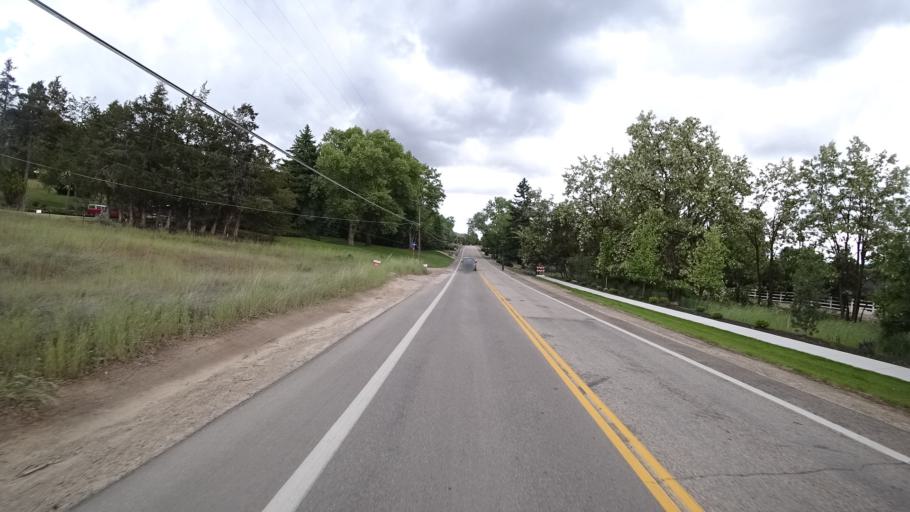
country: US
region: Idaho
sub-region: Ada County
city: Garden City
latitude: 43.6761
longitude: -116.2639
